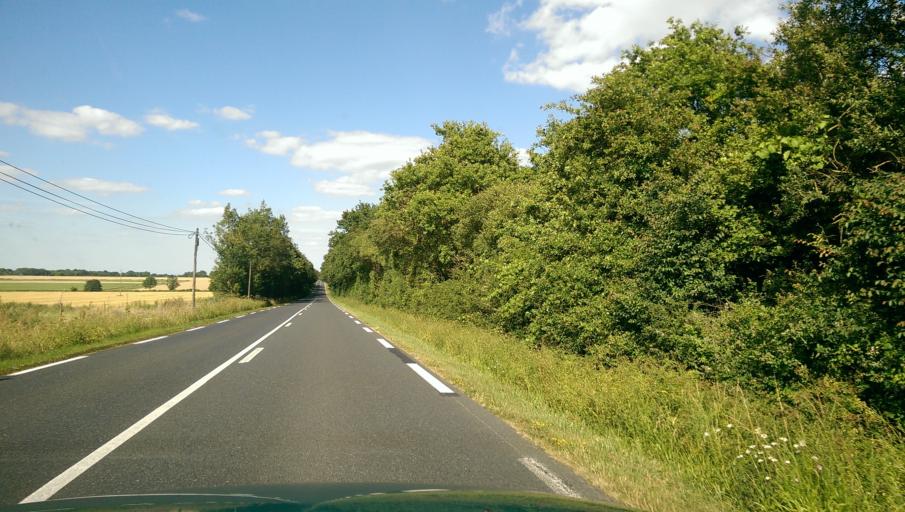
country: FR
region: Pays de la Loire
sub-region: Departement de la Vendee
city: Rocheserviere
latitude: 46.9474
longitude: -1.4881
